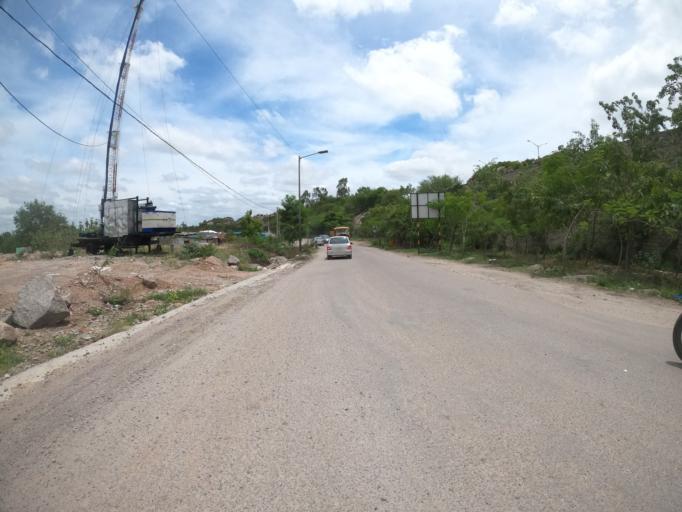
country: IN
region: Telangana
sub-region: Hyderabad
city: Hyderabad
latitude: 17.3087
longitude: 78.3769
